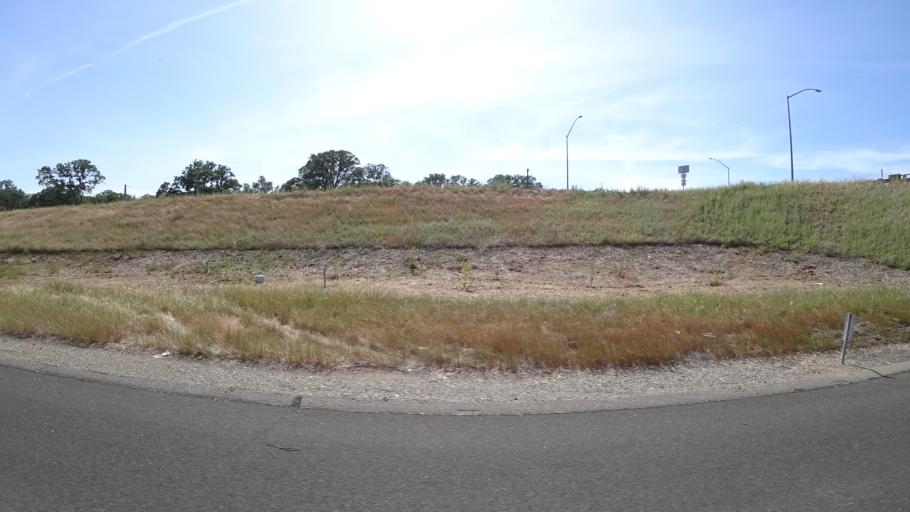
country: US
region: California
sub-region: Tehama County
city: Red Bluff
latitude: 40.2190
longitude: -122.2518
